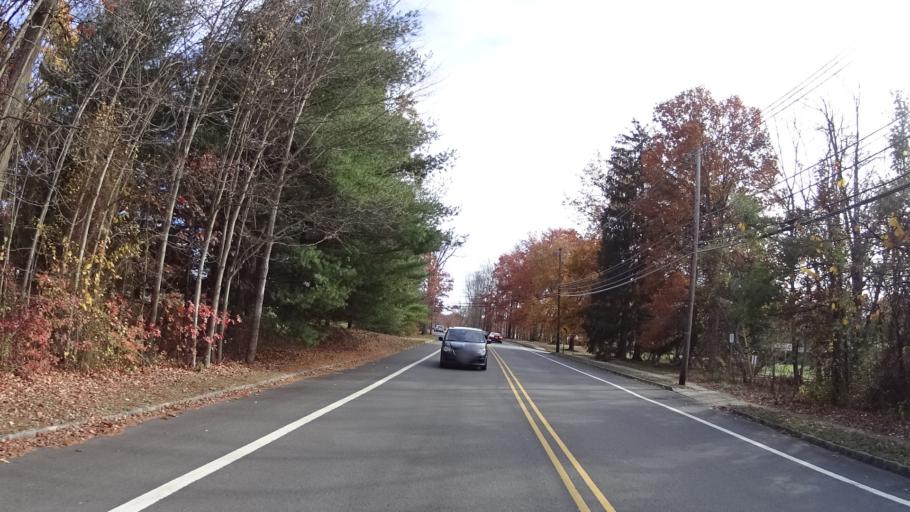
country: US
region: New Jersey
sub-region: Morris County
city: Madison
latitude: 40.7393
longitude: -74.4285
